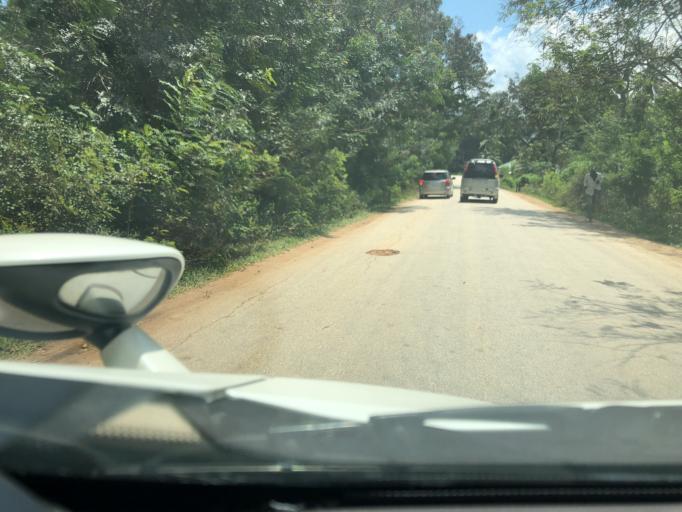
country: TZ
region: Zanzibar Central/South
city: Koani
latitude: -6.0604
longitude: 39.2522
